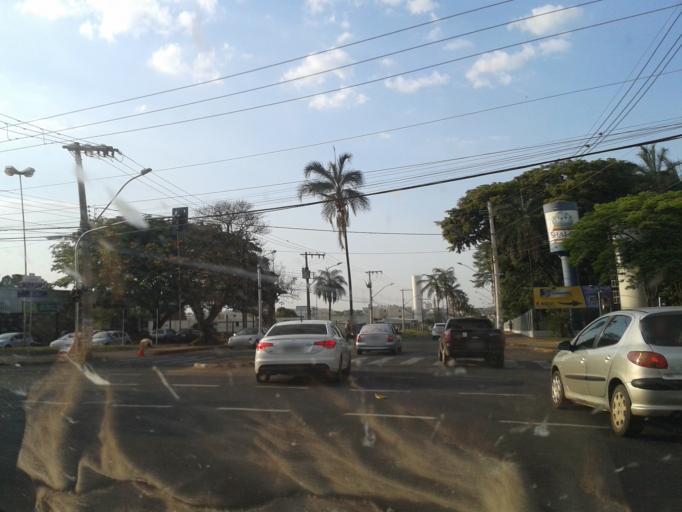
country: BR
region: Minas Gerais
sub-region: Uberlandia
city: Uberlandia
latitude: -18.9295
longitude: -48.3202
